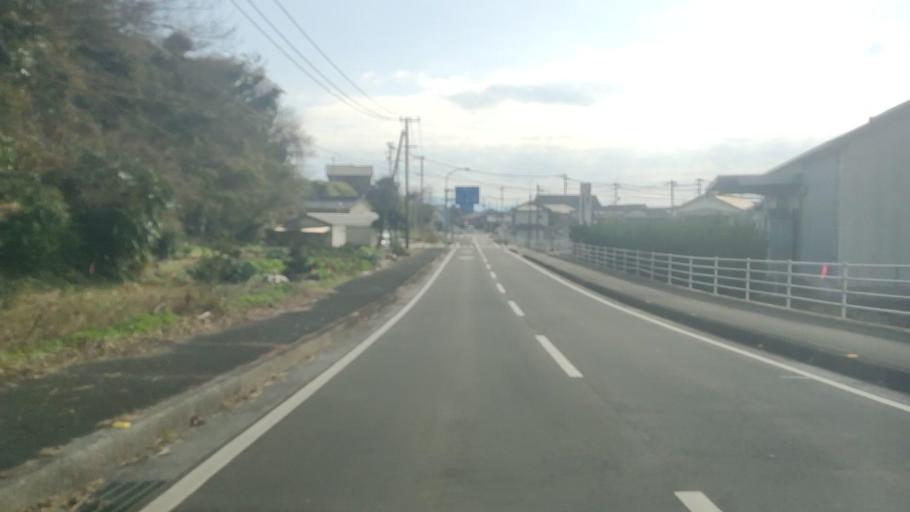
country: JP
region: Nagasaki
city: Shimabara
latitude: 32.6562
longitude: 130.2884
